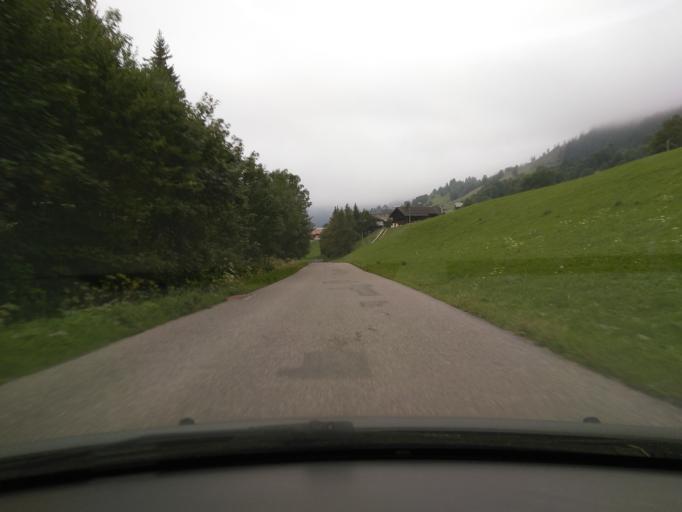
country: FR
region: Rhone-Alpes
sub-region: Departement de la Haute-Savoie
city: Le Grand-Bornand
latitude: 45.9135
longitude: 6.4648
